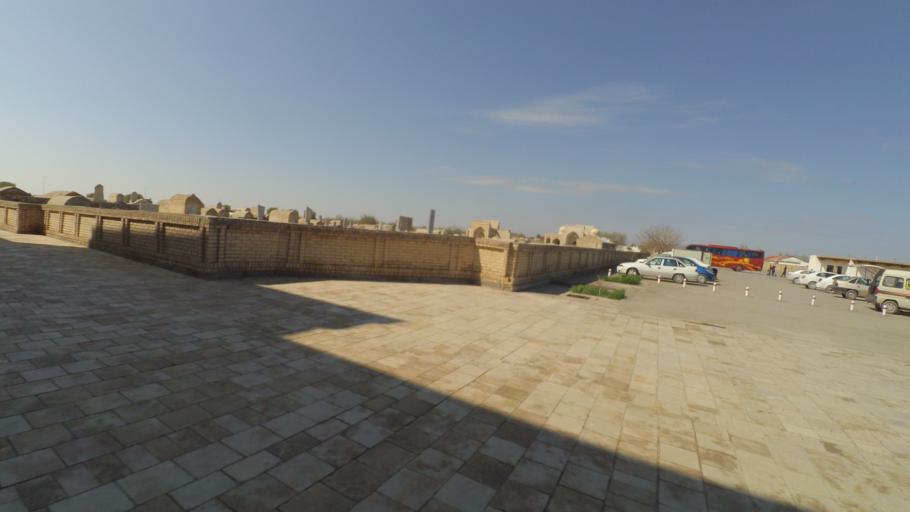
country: UZ
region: Bukhara
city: Kogon
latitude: 39.8019
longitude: 64.5365
